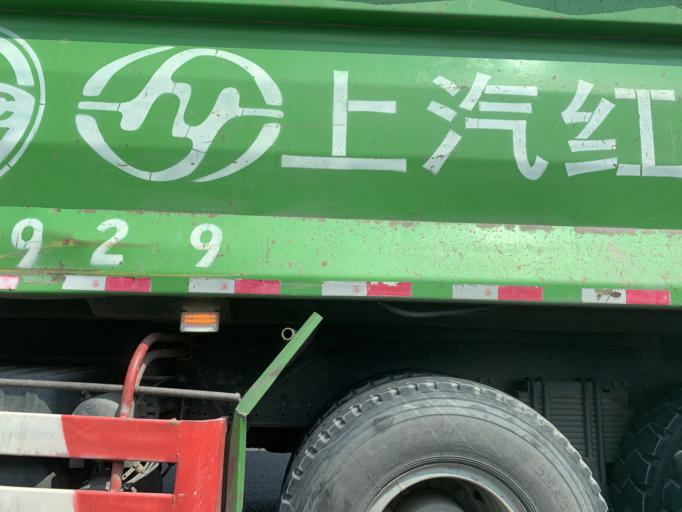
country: CN
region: Shanghai Shi
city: Huamu
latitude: 31.1884
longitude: 121.5062
